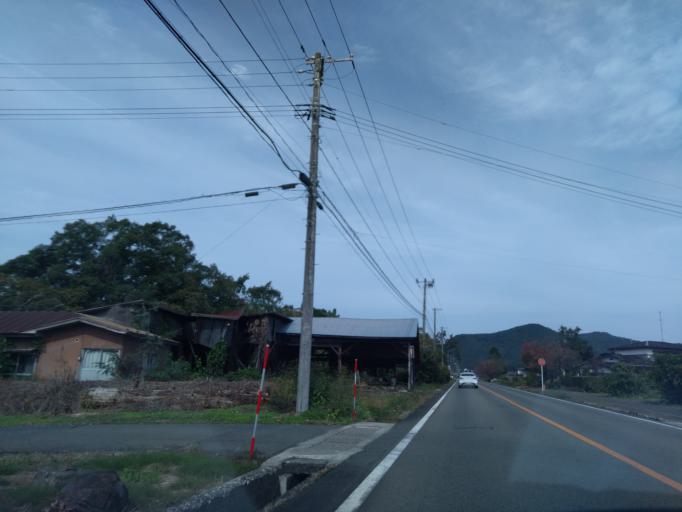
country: JP
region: Iwate
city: Hanamaki
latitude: 39.4380
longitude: 141.0789
